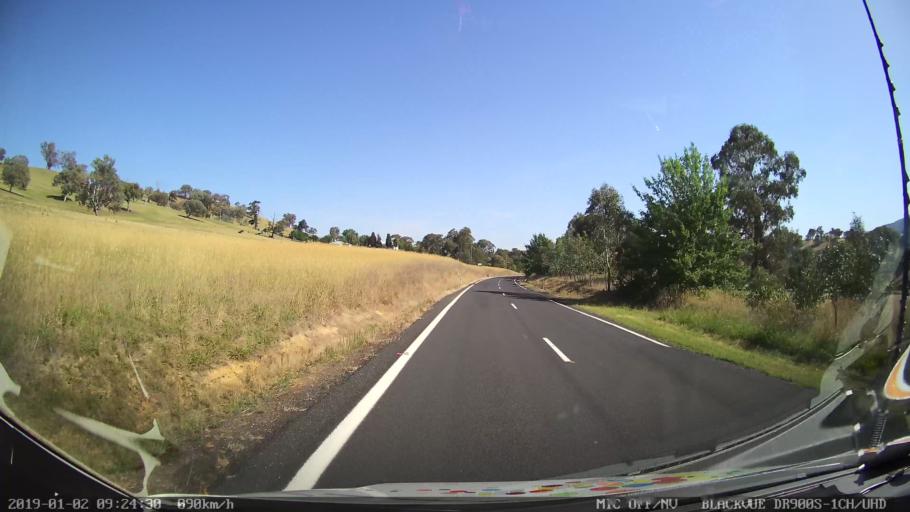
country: AU
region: New South Wales
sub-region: Tumut Shire
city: Tumut
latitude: -35.3762
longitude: 148.2918
